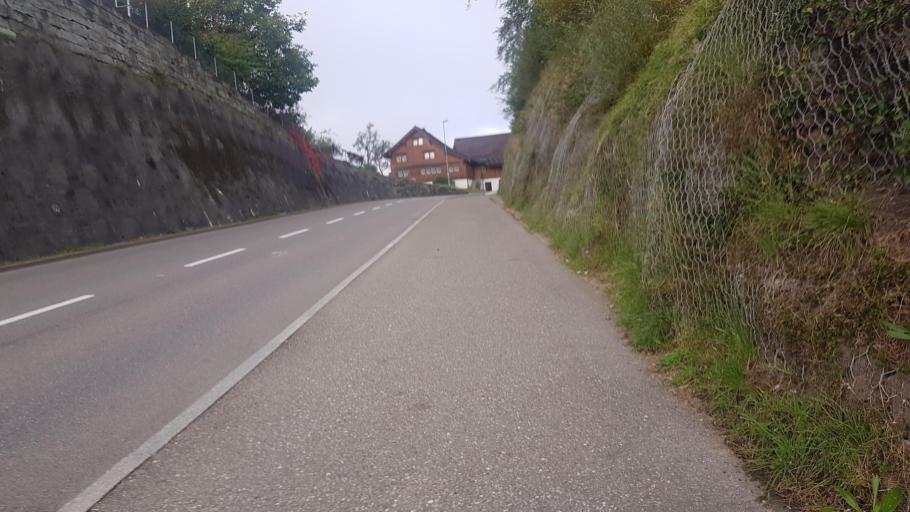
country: CH
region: Appenzell Ausserrhoden
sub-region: Bezirk Vorderland
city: Heiden
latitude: 47.4715
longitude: 9.5521
